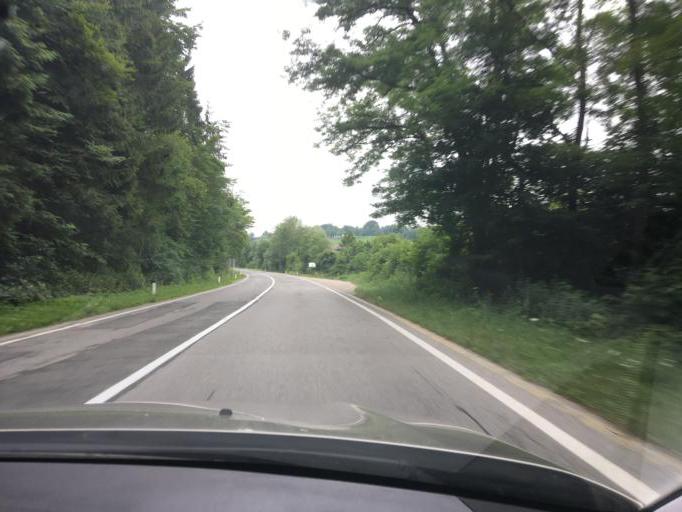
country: SI
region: Skofljica
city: Skofljica
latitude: 45.9838
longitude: 14.5857
